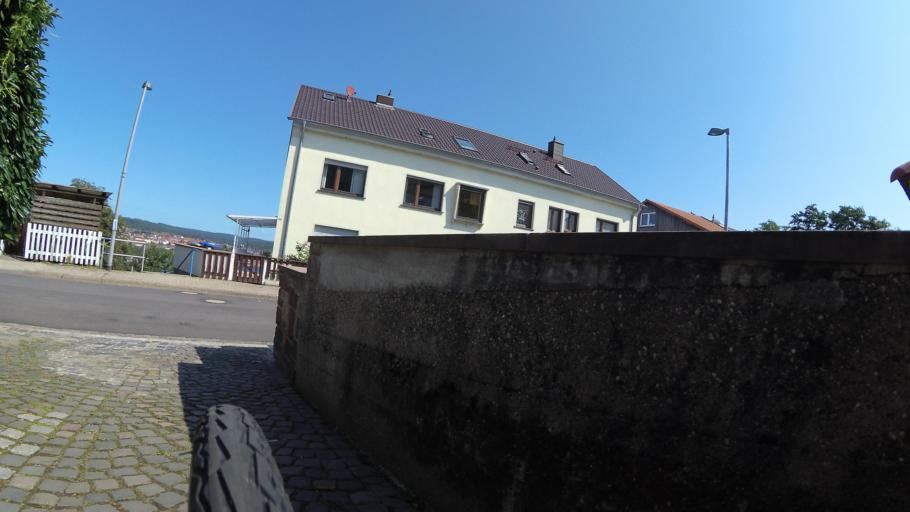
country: DE
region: Saarland
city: Saarbrucken
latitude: 49.2294
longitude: 6.9700
